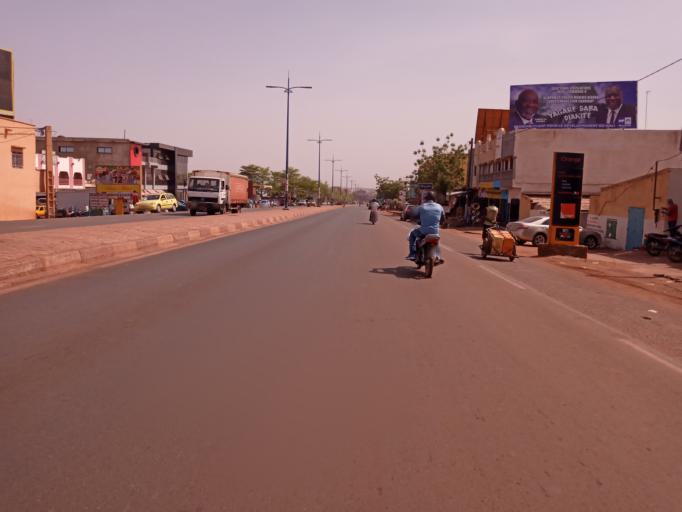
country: ML
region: Bamako
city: Bamako
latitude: 12.5877
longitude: -7.9919
